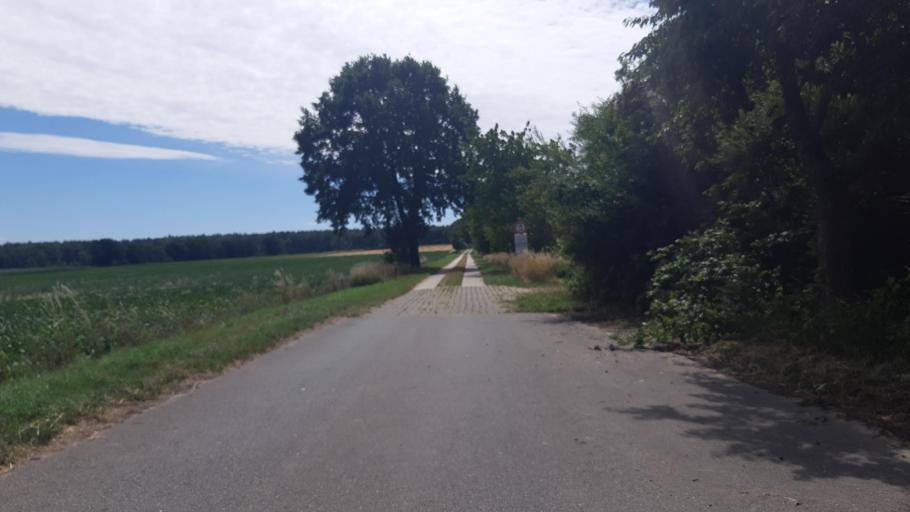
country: DE
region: Lower Saxony
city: Tosterglope
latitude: 53.2344
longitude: 10.7868
